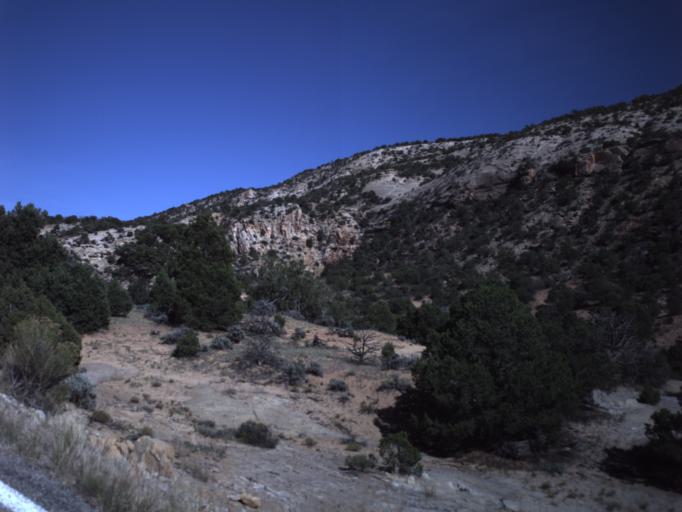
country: US
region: Utah
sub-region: San Juan County
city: Monticello
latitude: 37.9861
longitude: -109.4983
